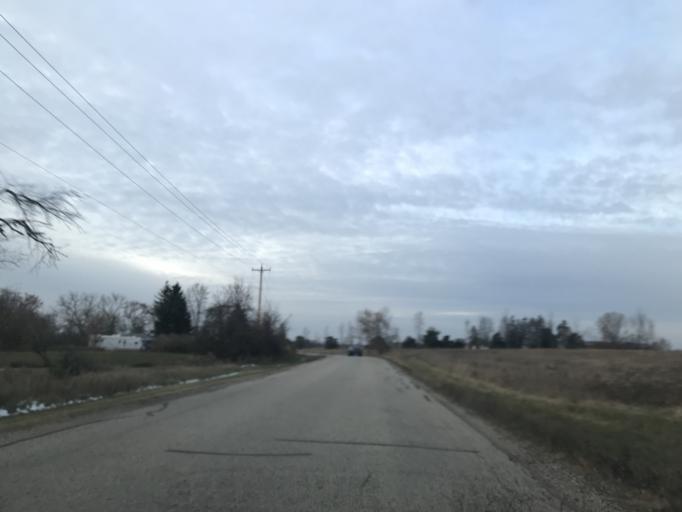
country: US
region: Wisconsin
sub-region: Marinette County
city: Peshtigo
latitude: 45.0555
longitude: -87.7977
